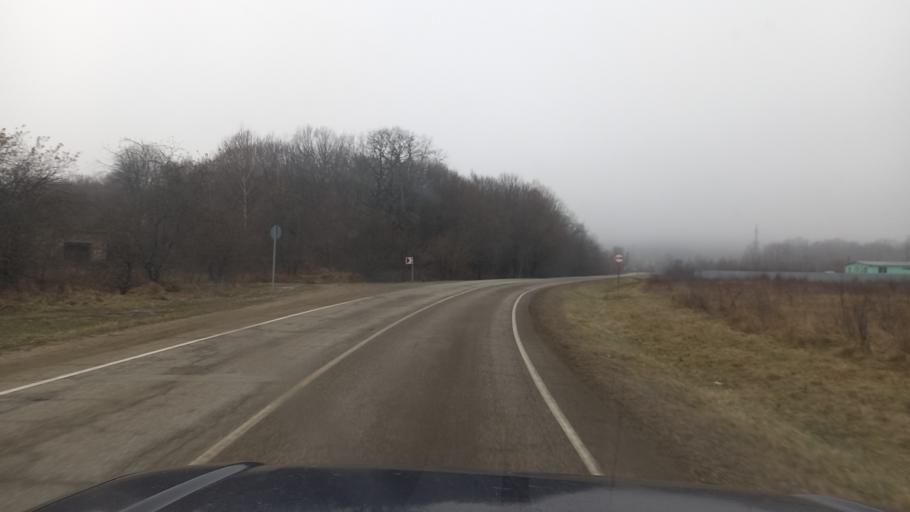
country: RU
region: Krasnodarskiy
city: Neftegorsk
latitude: 44.2876
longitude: 39.8194
